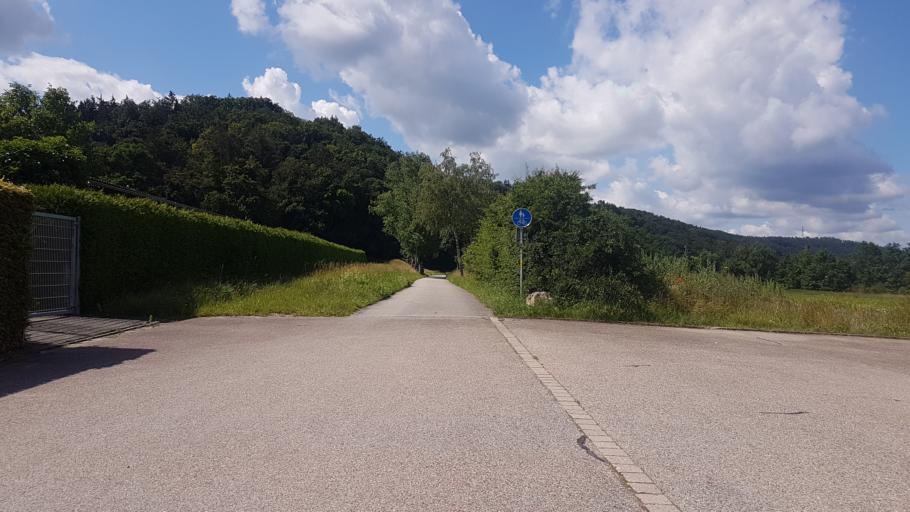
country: DE
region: Bavaria
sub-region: Upper Bavaria
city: Walting
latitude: 48.8862
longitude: 11.2602
